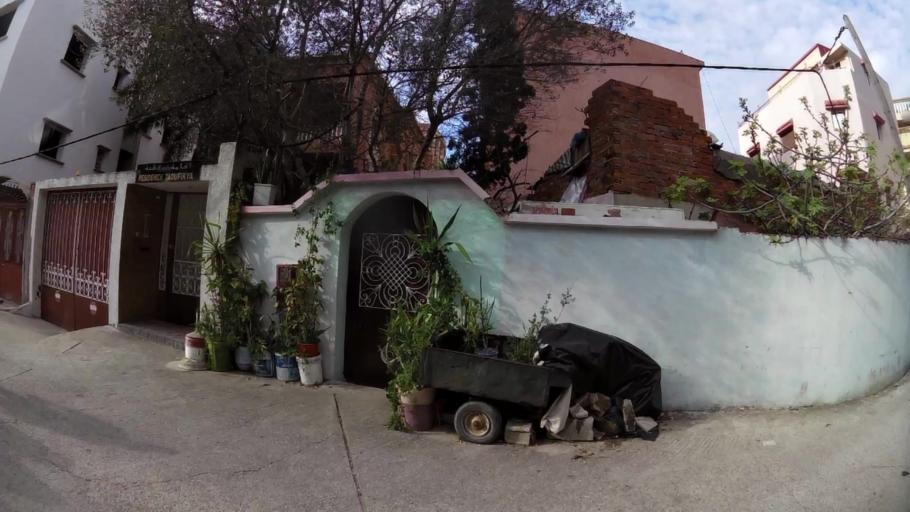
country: MA
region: Tanger-Tetouan
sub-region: Tanger-Assilah
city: Tangier
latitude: 35.7676
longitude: -5.7906
